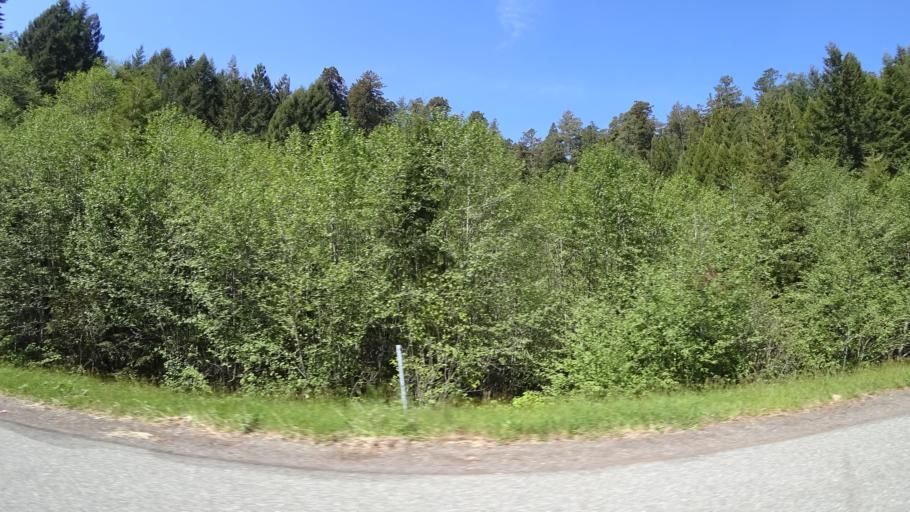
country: US
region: California
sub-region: Del Norte County
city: Bertsch-Oceanview
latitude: 41.4097
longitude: -124.0032
